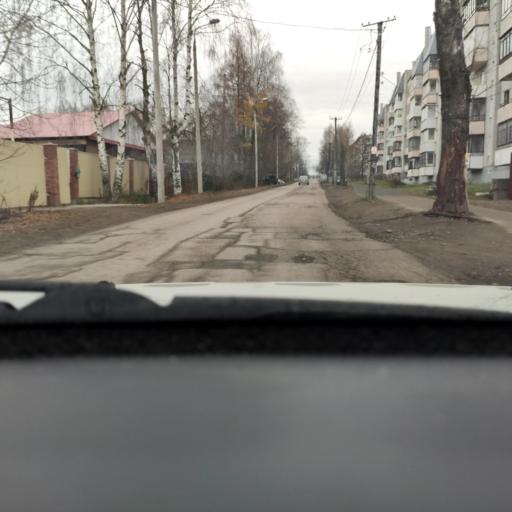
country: RU
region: Perm
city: Polazna
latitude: 58.1297
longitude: 56.3899
